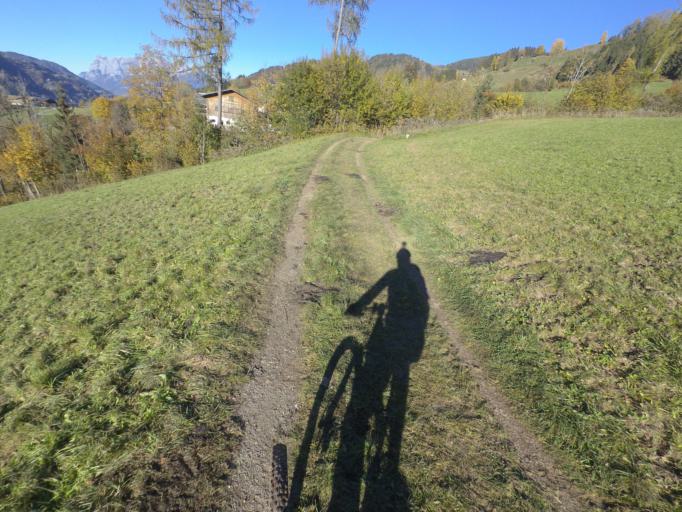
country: AT
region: Salzburg
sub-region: Politischer Bezirk Sankt Johann im Pongau
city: Sankt Johann im Pongau
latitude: 47.3468
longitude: 13.2185
